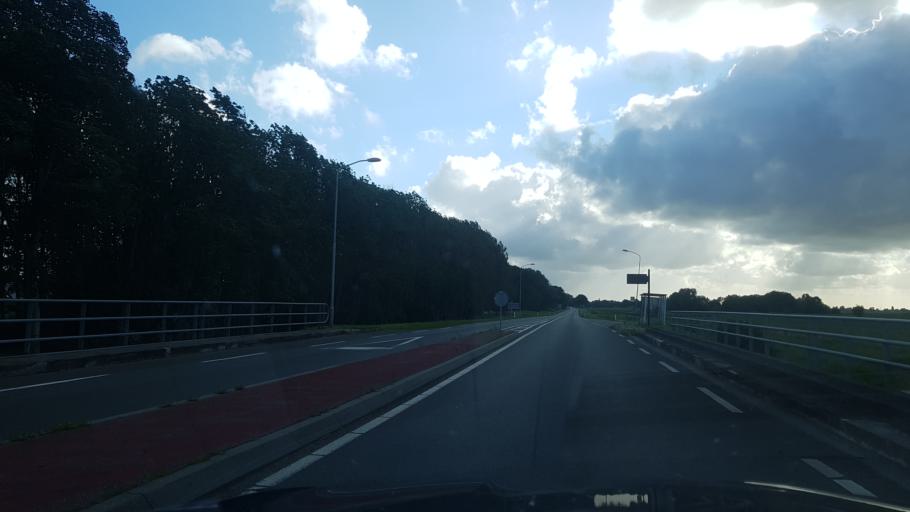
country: NL
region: Groningen
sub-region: Gemeente Appingedam
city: Appingedam
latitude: 53.3128
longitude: 6.7698
